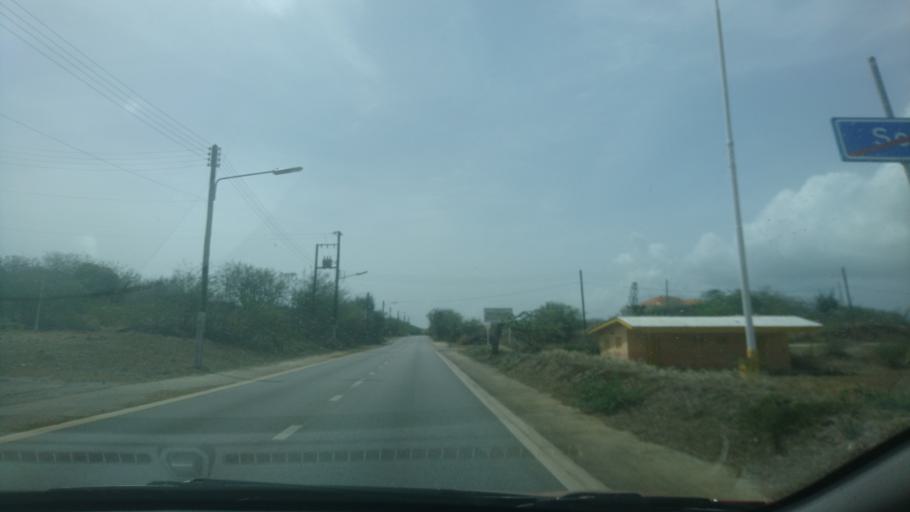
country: CW
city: Dorp Soto
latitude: 12.2738
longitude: -69.1070
